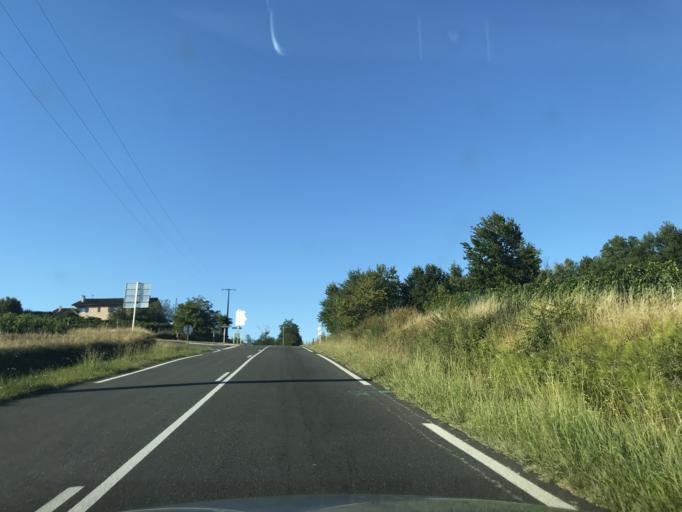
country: FR
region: Aquitaine
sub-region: Departement de la Gironde
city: Saint-Macaire
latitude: 44.5784
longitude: -0.2156
